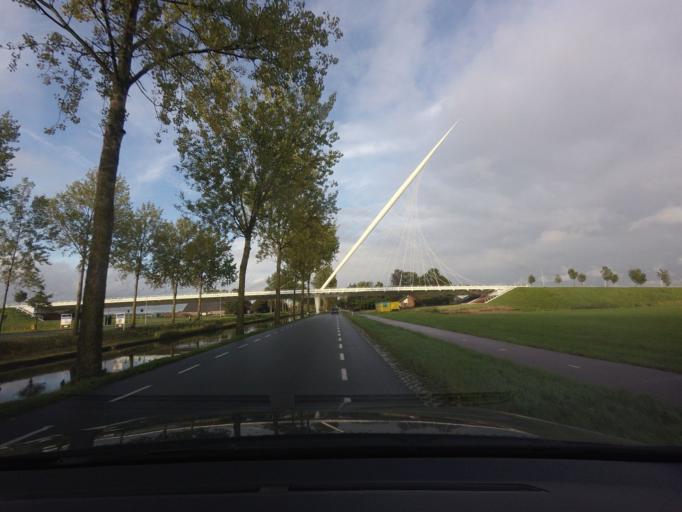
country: NL
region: North Holland
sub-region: Gemeente Haarlemmermeer
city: Hoofddorp
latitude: 52.2721
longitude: 4.6451
